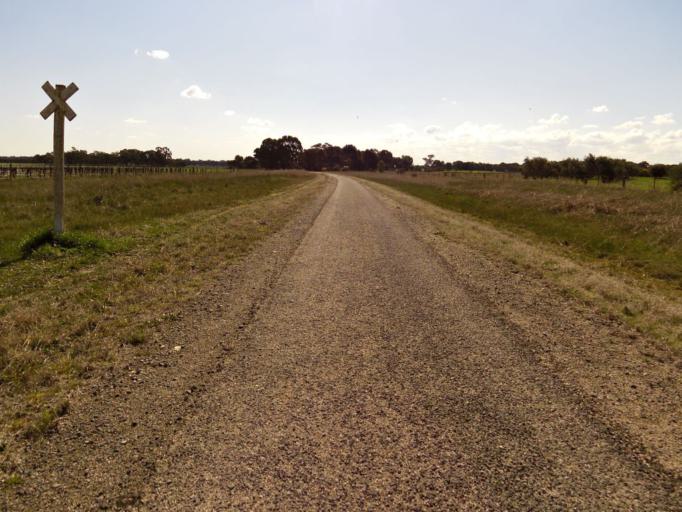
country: AU
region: New South Wales
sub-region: Corowa Shire
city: Corowa
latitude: -36.0397
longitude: 146.4535
